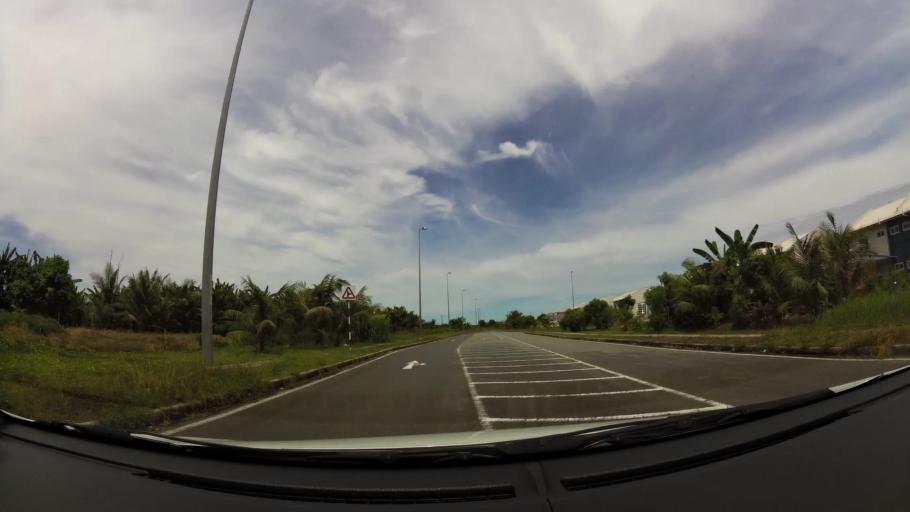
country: BN
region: Belait
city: Kuala Belait
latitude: 4.5859
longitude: 114.2676
